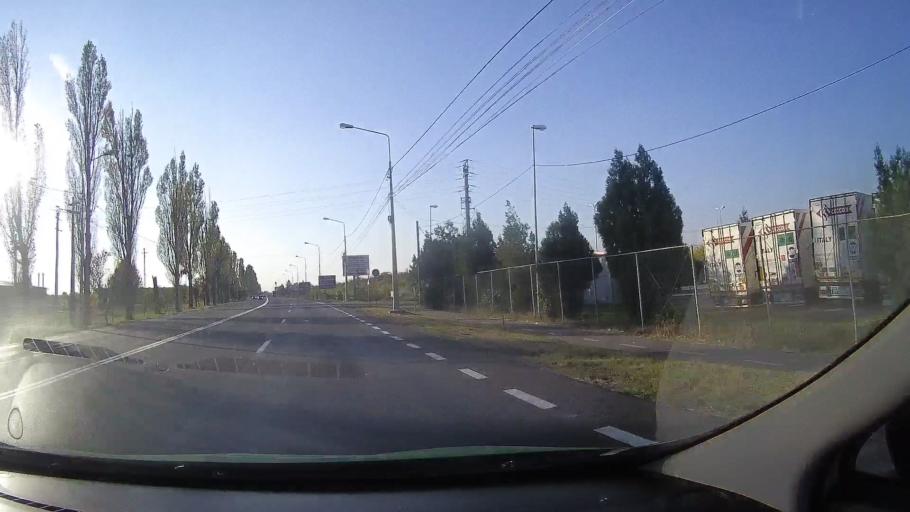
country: RO
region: Bihor
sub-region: Comuna Bors
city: Santion
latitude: 47.0993
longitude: 21.8567
